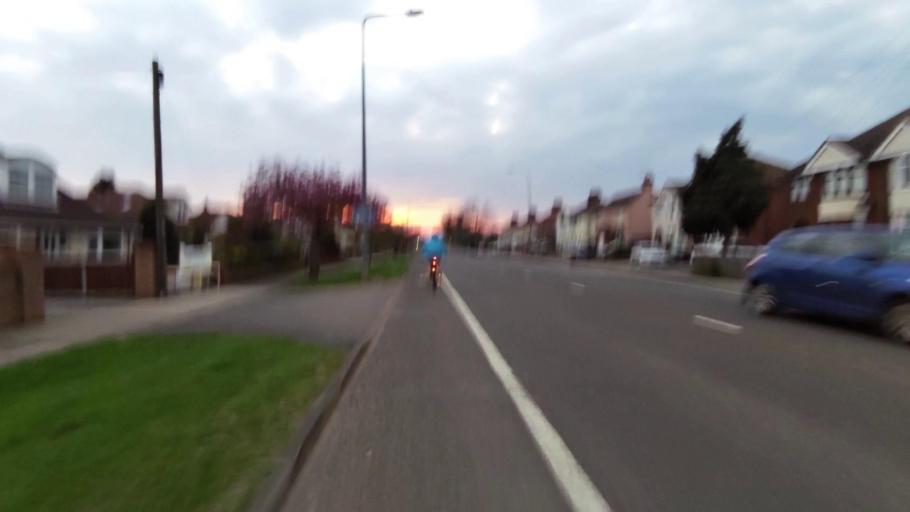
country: GB
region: England
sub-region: Suffolk
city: Ipswich
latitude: 52.0677
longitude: 1.1859
